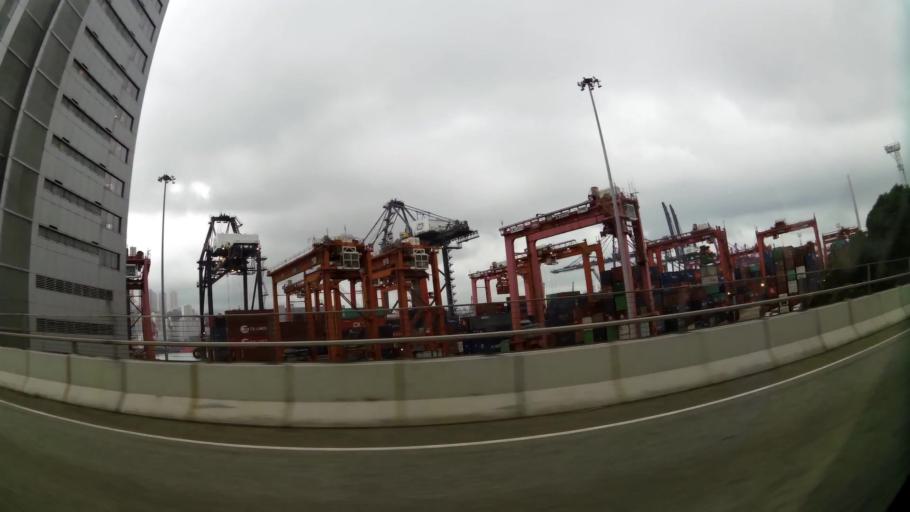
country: HK
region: Tsuen Wan
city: Tsuen Wan
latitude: 22.3436
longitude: 114.1115
